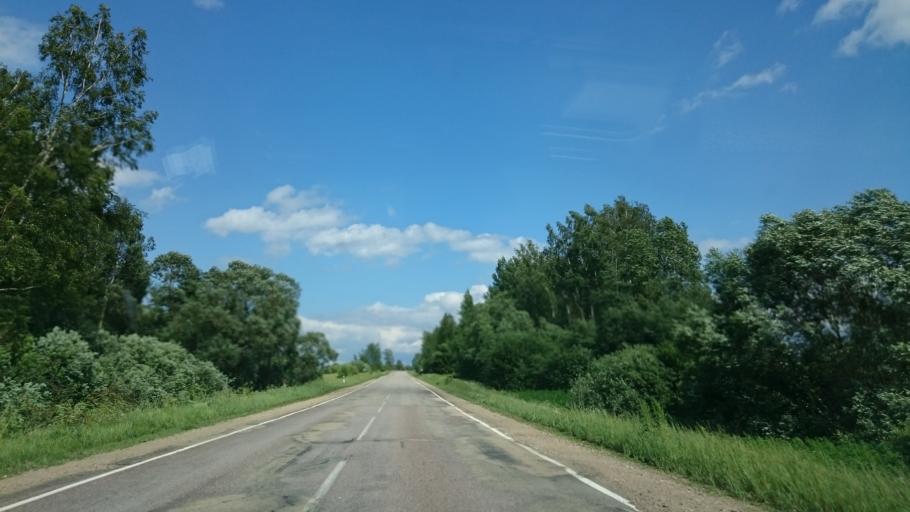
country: LV
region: Ludzas Rajons
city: Ludza
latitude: 56.5350
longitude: 27.6115
